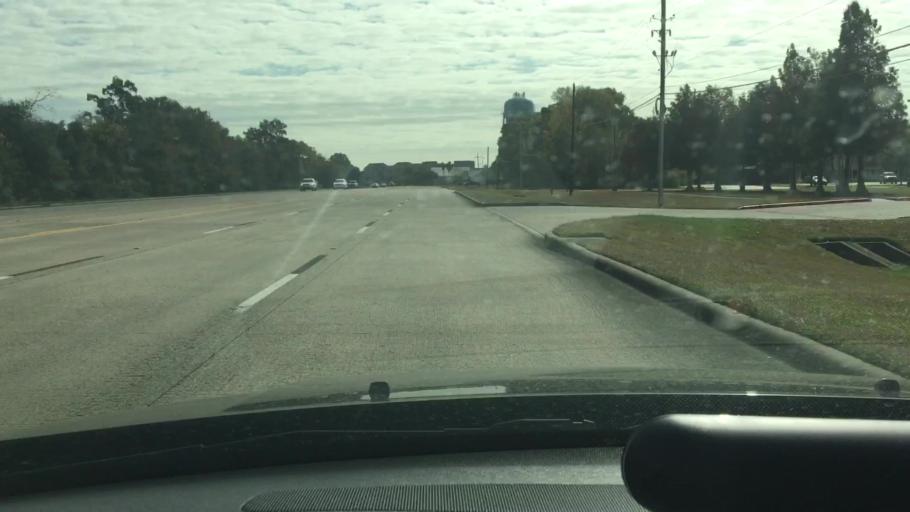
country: US
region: Texas
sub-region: Harris County
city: Nassau Bay
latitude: 29.5266
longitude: -95.0876
